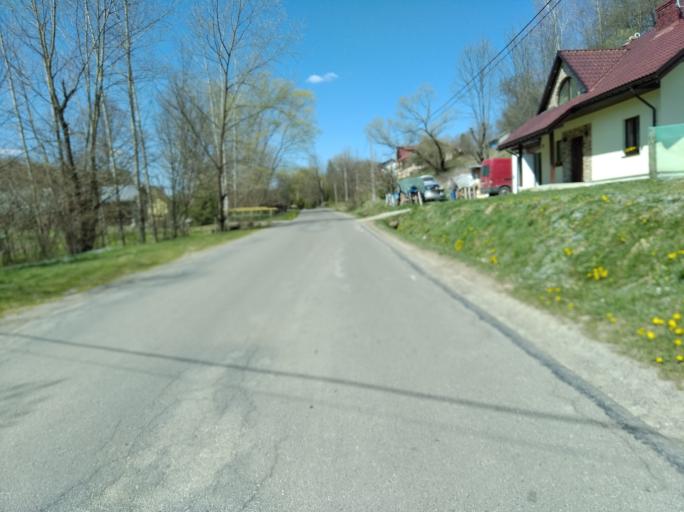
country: PL
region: Subcarpathian Voivodeship
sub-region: Powiat brzozowski
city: Jablonka
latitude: 49.7116
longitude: 22.1401
